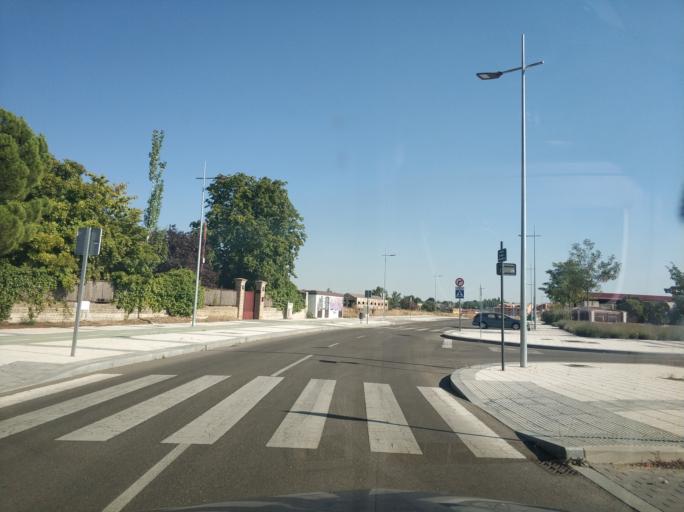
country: ES
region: Castille and Leon
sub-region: Provincia de Burgos
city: Aranda de Duero
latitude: 41.6695
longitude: -3.6962
